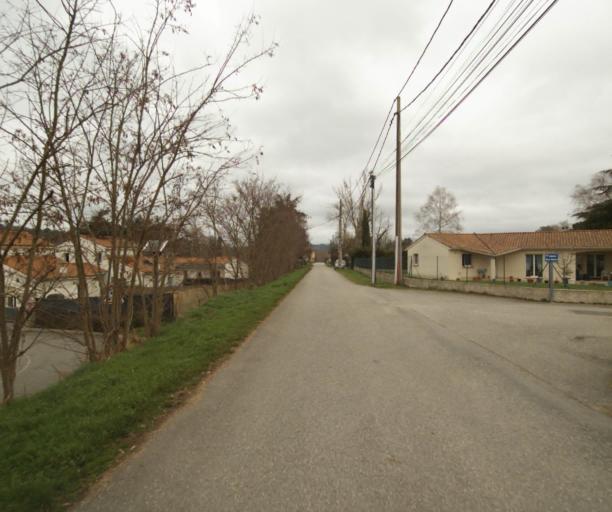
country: FR
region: Midi-Pyrenees
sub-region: Departement de l'Ariege
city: Pamiers
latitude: 43.1352
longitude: 1.6023
